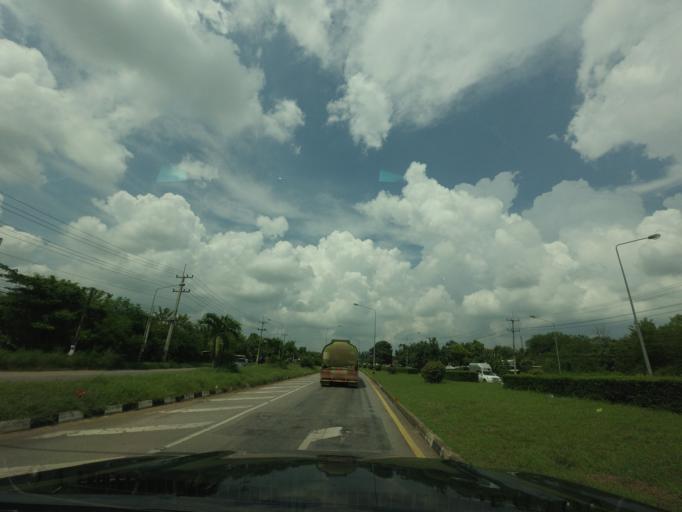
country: TH
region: Khon Kaen
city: Nong Ruea
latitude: 16.4883
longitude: 102.4074
